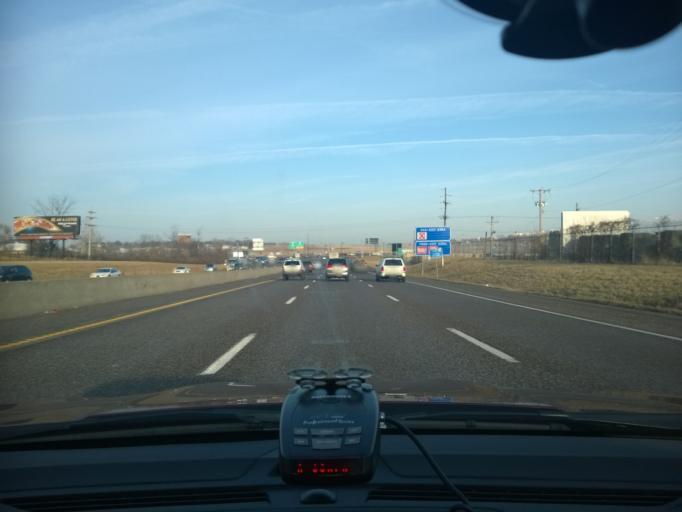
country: US
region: Missouri
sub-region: Saint Louis County
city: Saint Ann
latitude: 38.7420
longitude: -90.3763
